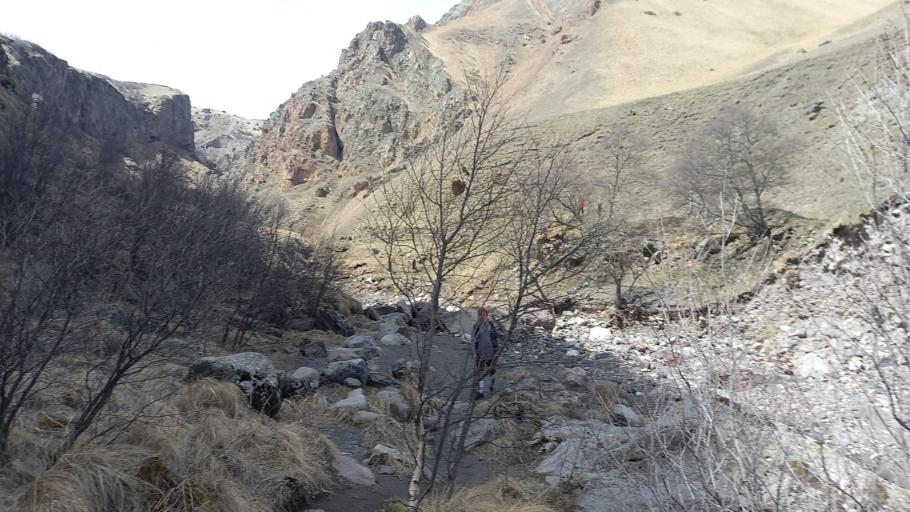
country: RU
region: Kabardino-Balkariya
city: Terskol
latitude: 43.4415
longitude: 42.5472
